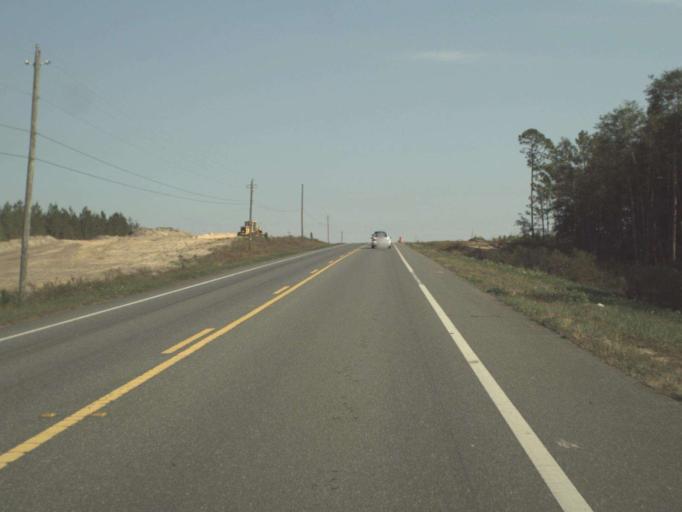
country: US
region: Florida
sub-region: Holmes County
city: Bonifay
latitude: 30.6889
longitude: -85.6863
